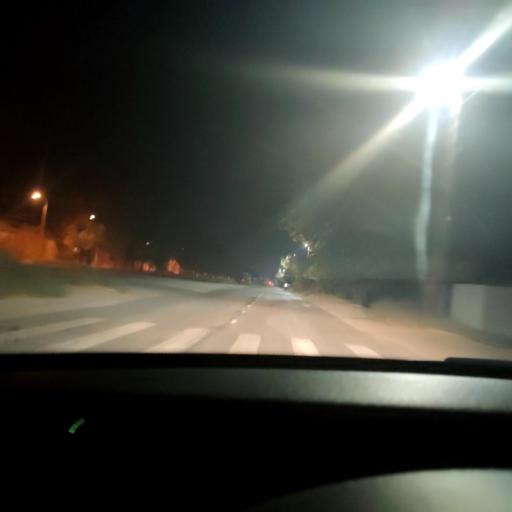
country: RU
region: Samara
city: Petra-Dubrava
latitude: 53.2368
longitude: 50.3081
